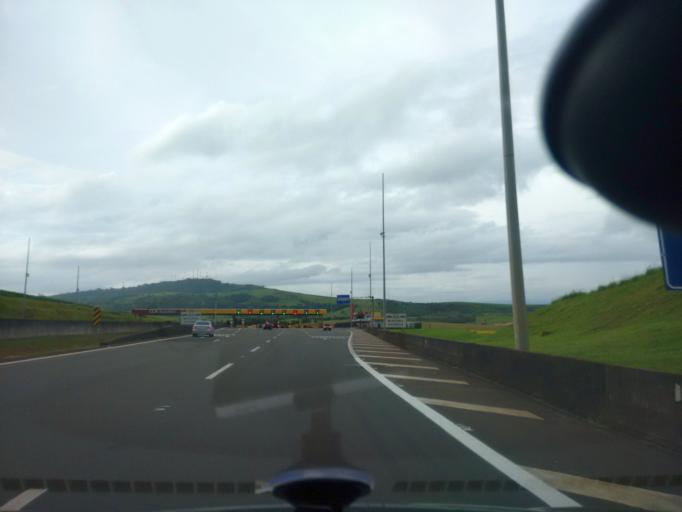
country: BR
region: Sao Paulo
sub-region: Limeira
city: Limeira
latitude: -22.5580
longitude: -47.4597
